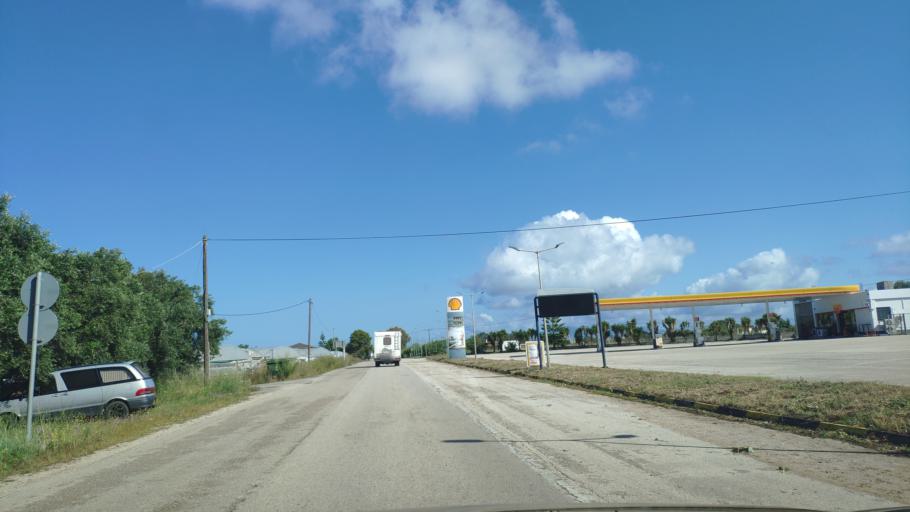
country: GR
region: Epirus
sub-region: Nomos Prevezis
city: Preveza
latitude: 38.9323
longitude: 20.7729
